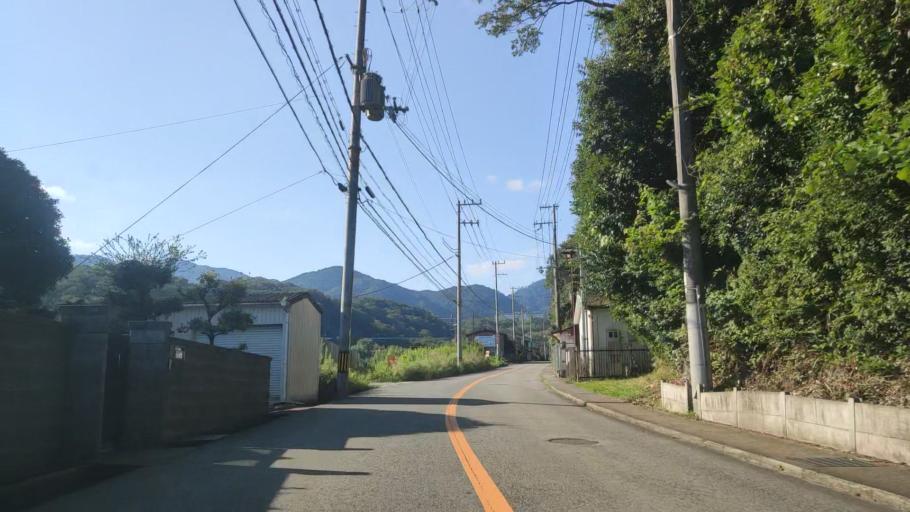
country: JP
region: Hyogo
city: Sandacho
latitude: 34.8094
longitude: 135.2505
